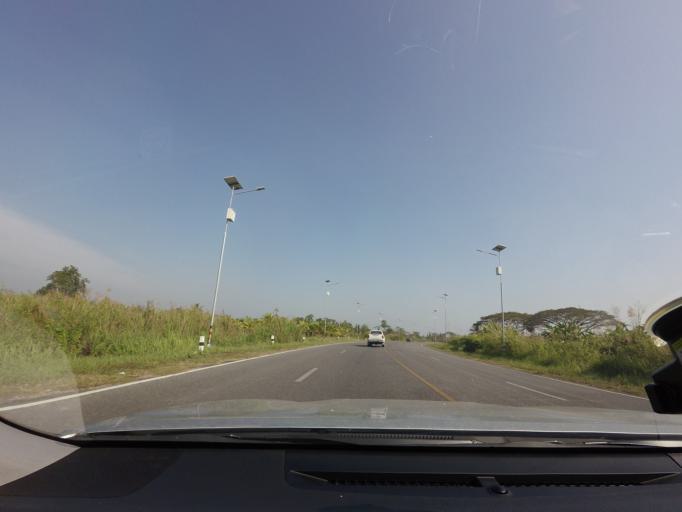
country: TH
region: Nakhon Si Thammarat
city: Nakhon Si Thammarat
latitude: 8.4839
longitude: 99.9759
